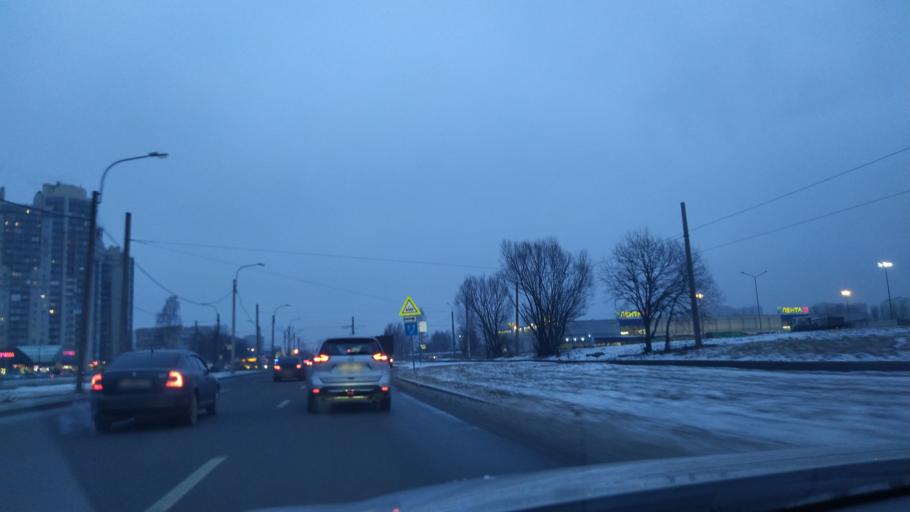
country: RU
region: Leningrad
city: Murino
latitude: 60.0290
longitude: 30.4322
